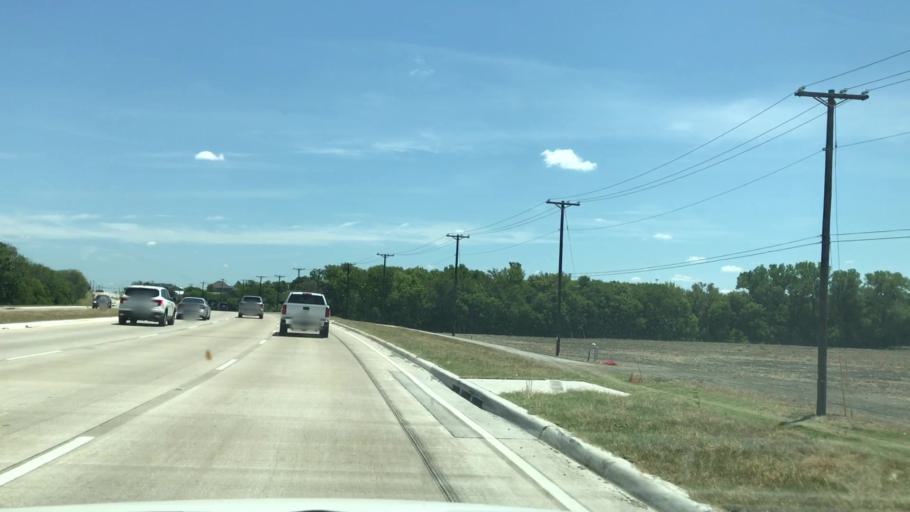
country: US
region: Texas
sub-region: Collin County
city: Lavon
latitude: 33.0216
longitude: -96.4702
